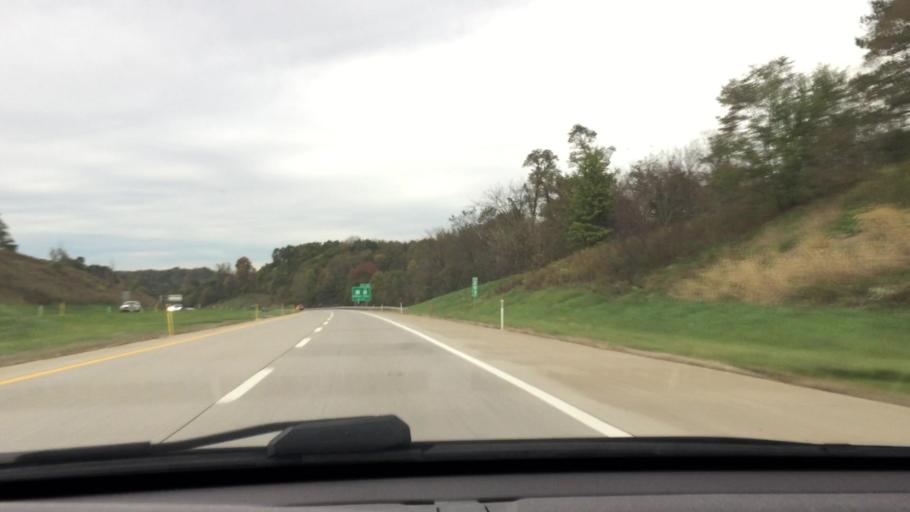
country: US
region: Pennsylvania
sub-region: Beaver County
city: West Mayfield
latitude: 40.7819
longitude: -80.3557
